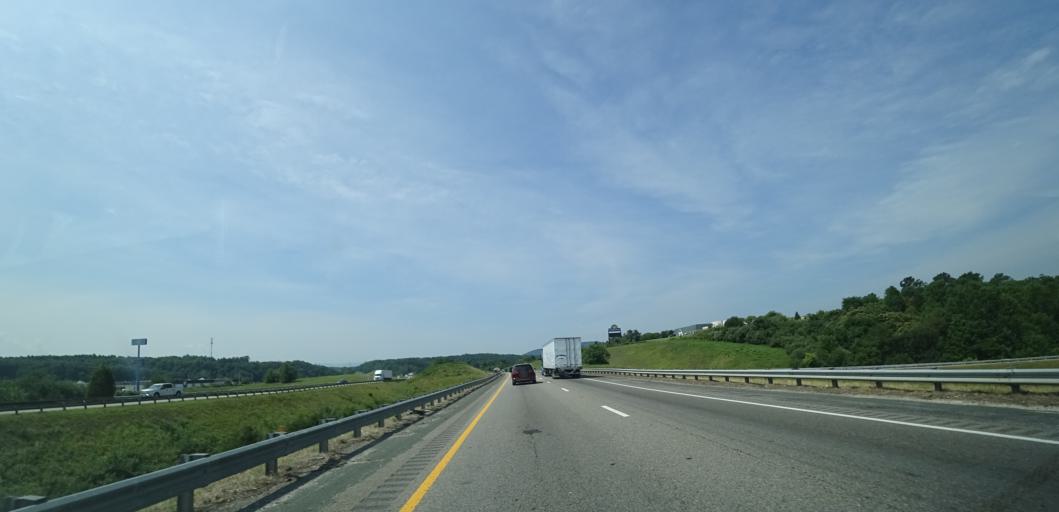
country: US
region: Virginia
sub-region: Augusta County
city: Verona
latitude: 38.1667
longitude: -79.0106
